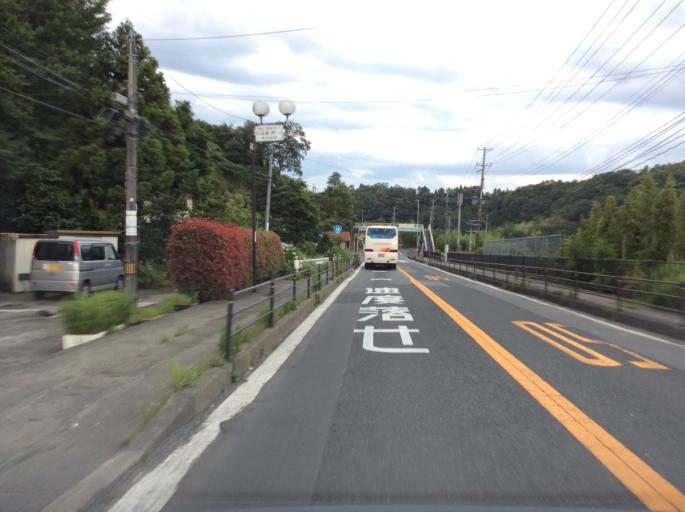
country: JP
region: Fukushima
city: Iwaki
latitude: 37.0728
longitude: 140.8280
